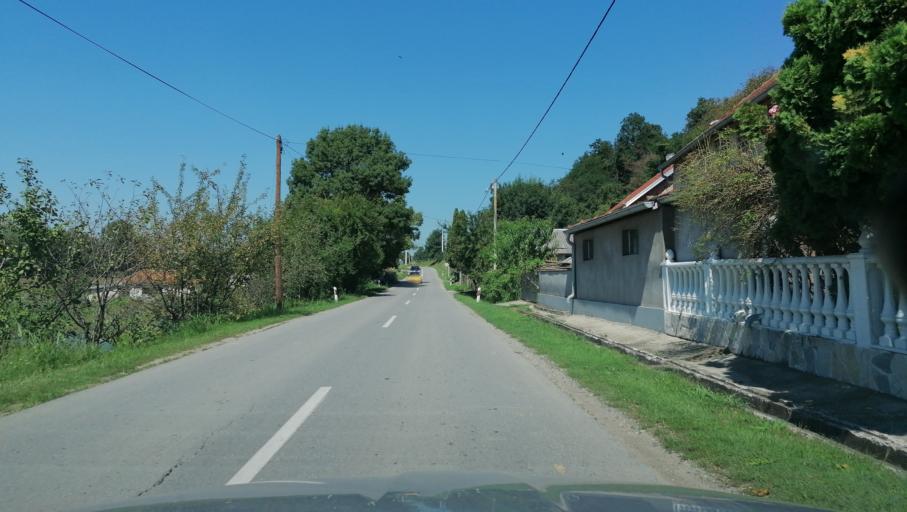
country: RS
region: Central Serbia
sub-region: Raski Okrug
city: Vrnjacka Banja
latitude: 43.6936
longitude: 20.8631
